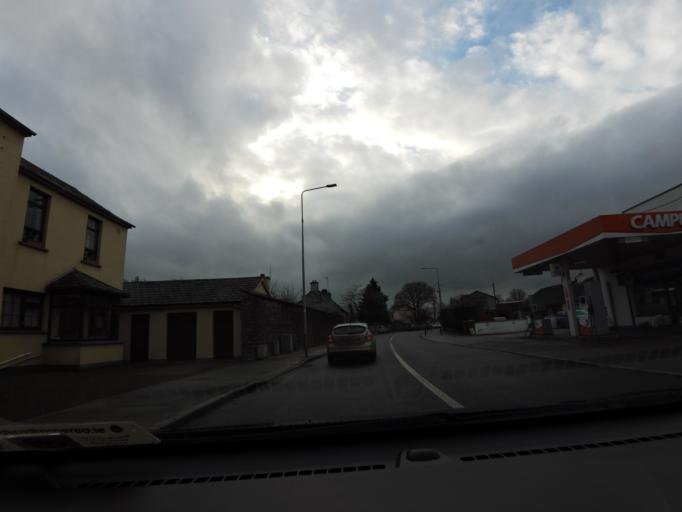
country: IE
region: Leinster
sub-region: Kilkenny
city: Ballyragget
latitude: 52.7887
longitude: -7.3327
